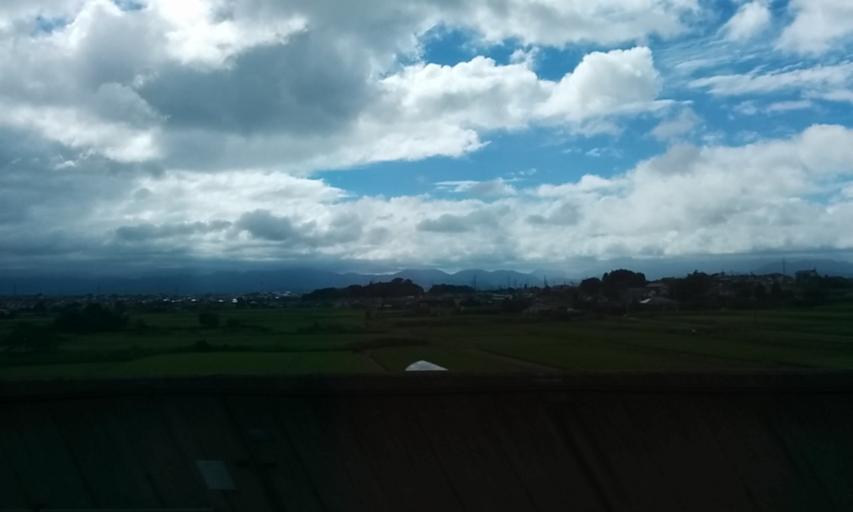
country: JP
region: Fukushima
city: Koriyama
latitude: 37.4439
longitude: 140.4036
